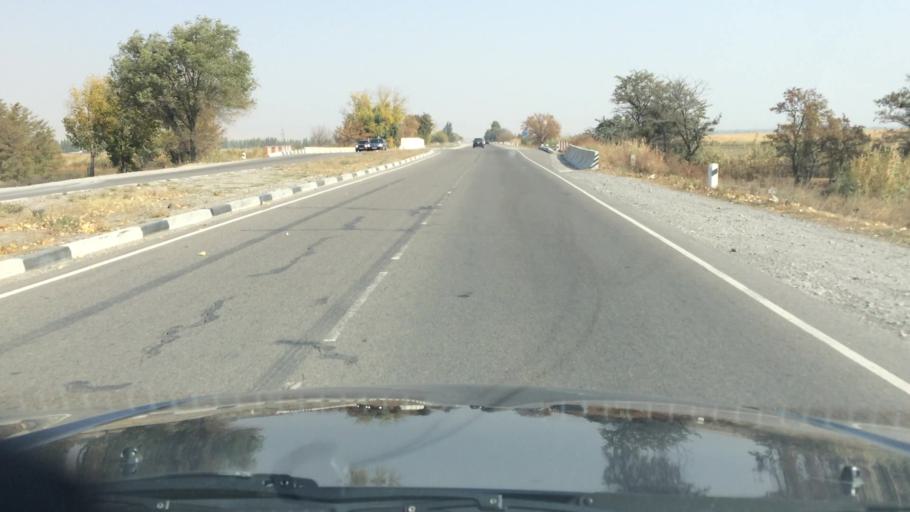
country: KG
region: Chuy
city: Kant
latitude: 42.9548
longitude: 74.7931
